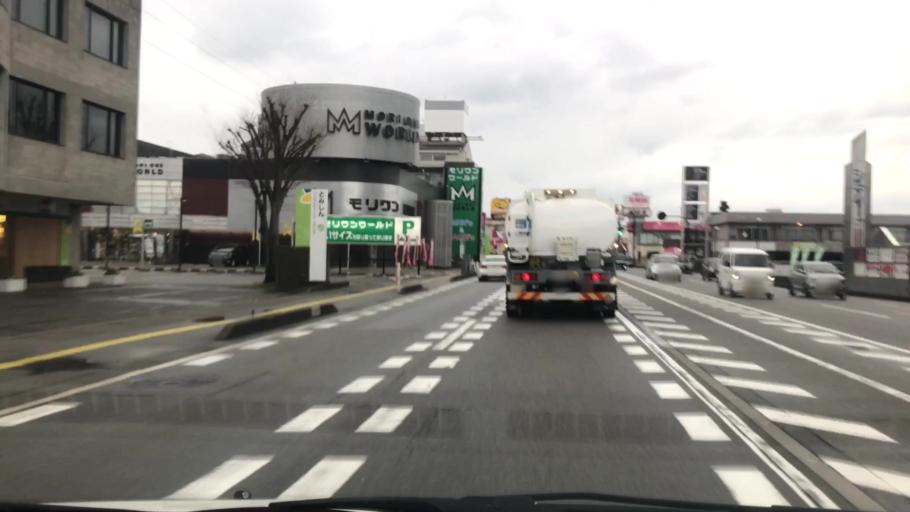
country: JP
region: Toyama
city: Toyama-shi
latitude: 36.6727
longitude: 137.2105
